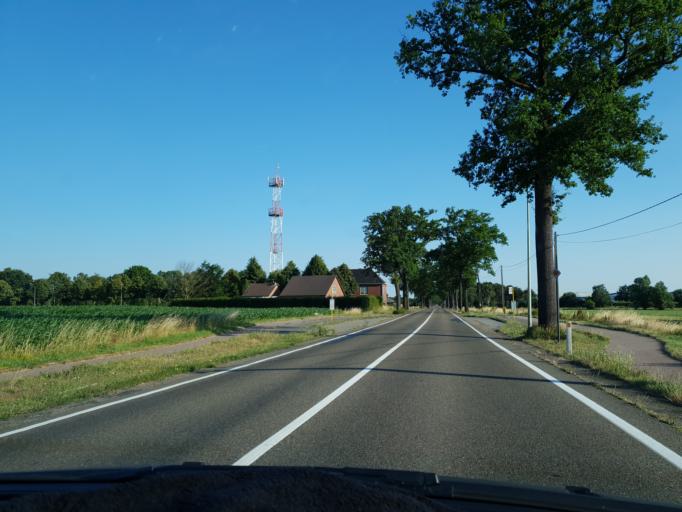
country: BE
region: Flanders
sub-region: Provincie Antwerpen
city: Hoogstraten
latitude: 51.3836
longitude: 4.7558
